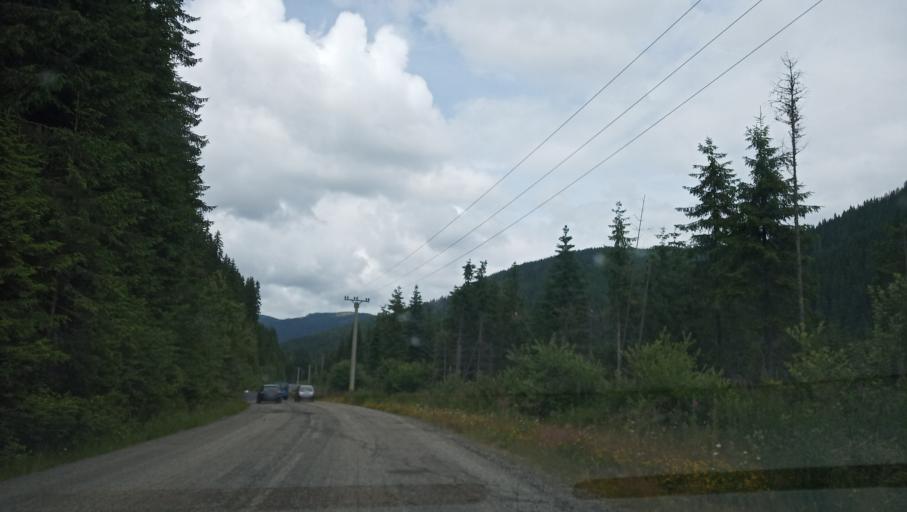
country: RO
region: Gorj
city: Novaci-Straini
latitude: 45.4306
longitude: 23.6749
